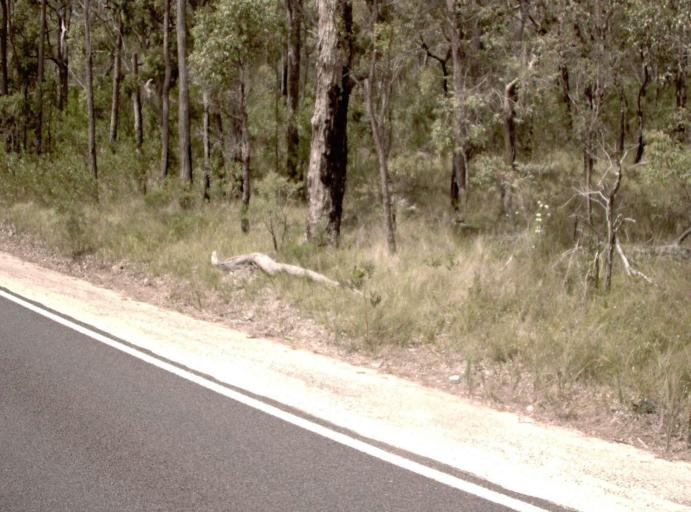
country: AU
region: New South Wales
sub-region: Bega Valley
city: Eden
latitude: -37.4347
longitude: 149.6450
